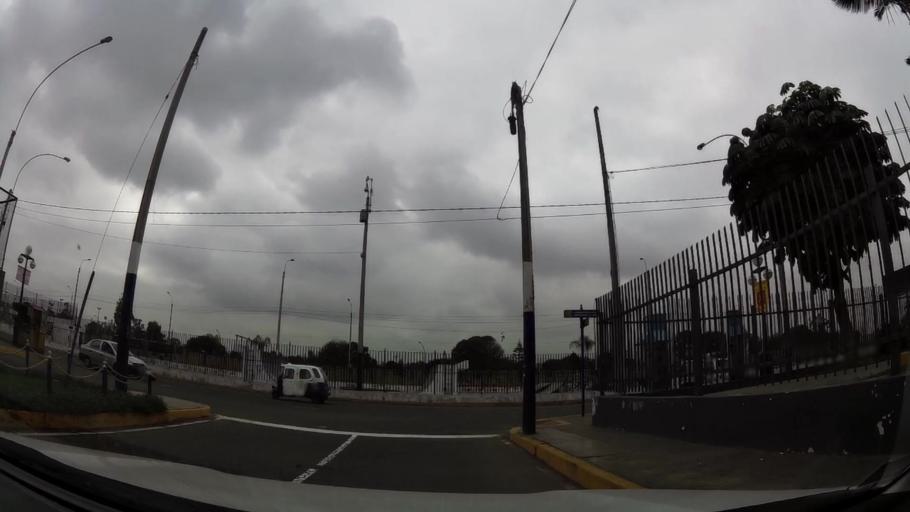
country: PE
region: Lima
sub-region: Lima
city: Surco
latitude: -12.1707
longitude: -77.0178
